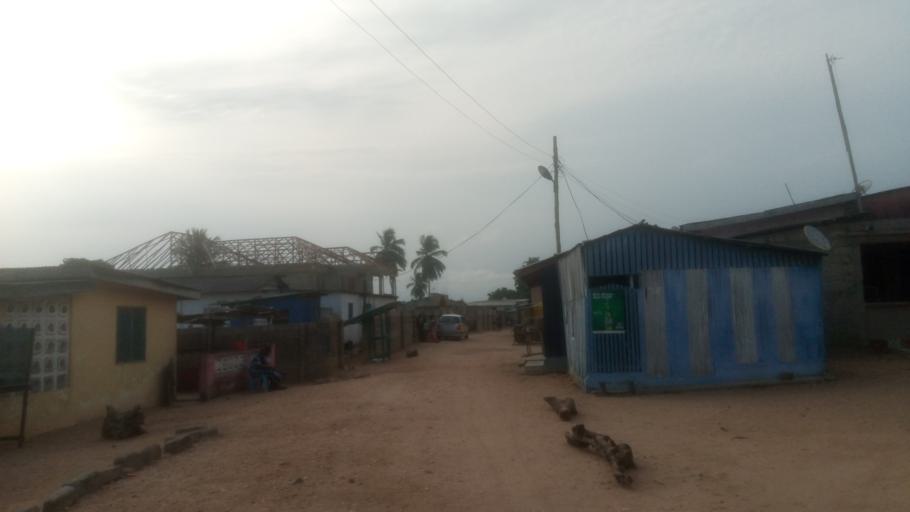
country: GH
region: Central
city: Winneba
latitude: 5.3532
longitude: -0.6278
